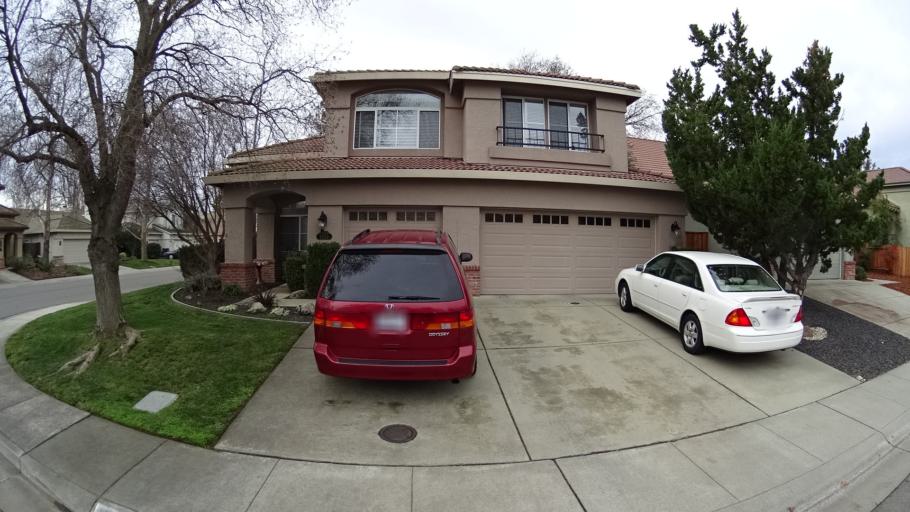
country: US
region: California
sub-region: Yolo County
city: Davis
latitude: 38.5558
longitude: -121.7148
